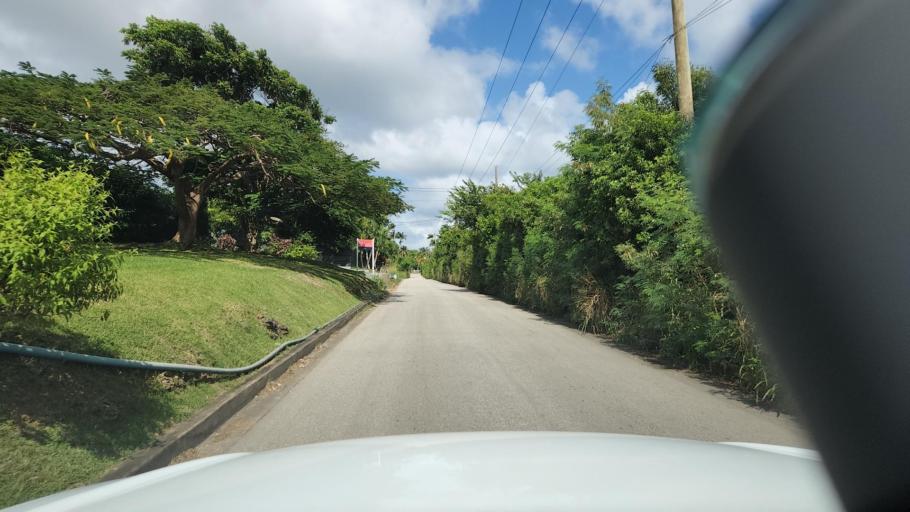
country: BB
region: Saint John
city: Four Cross Roads
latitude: 13.1642
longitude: -59.5034
